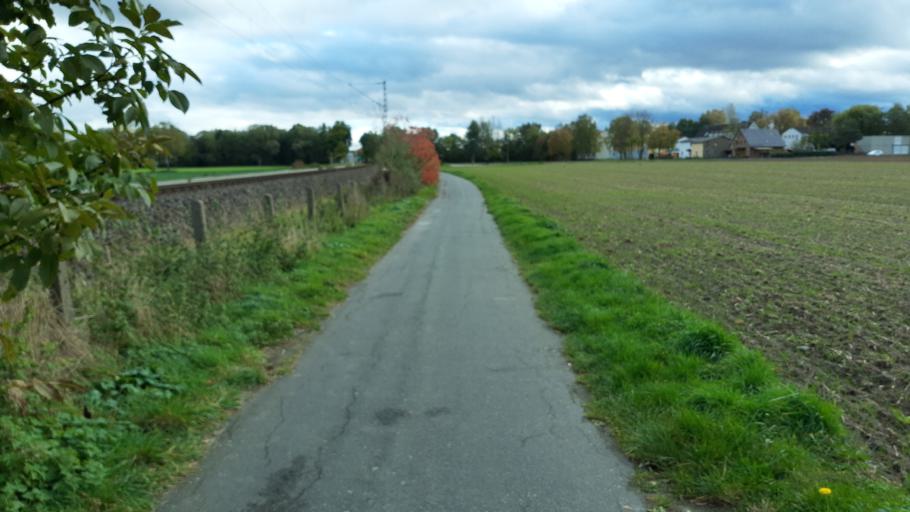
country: DE
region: North Rhine-Westphalia
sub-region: Regierungsbezirk Detmold
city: Detmold
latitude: 51.9497
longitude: 8.8381
